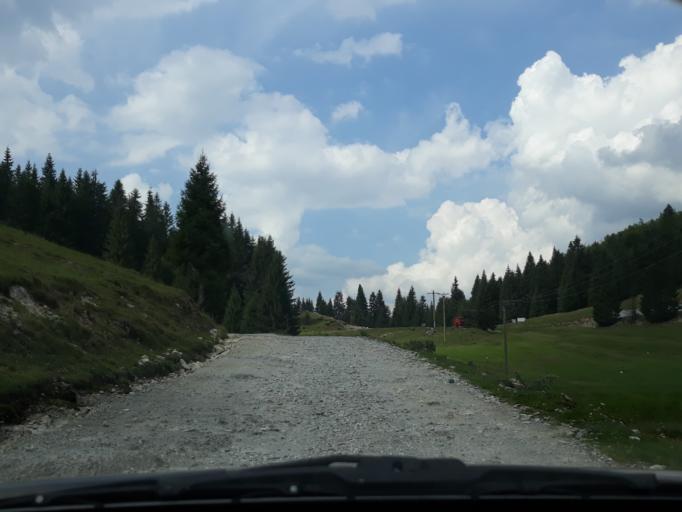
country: RO
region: Bihor
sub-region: Comuna Pietroasa
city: Pietroasa
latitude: 46.5906
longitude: 22.6850
